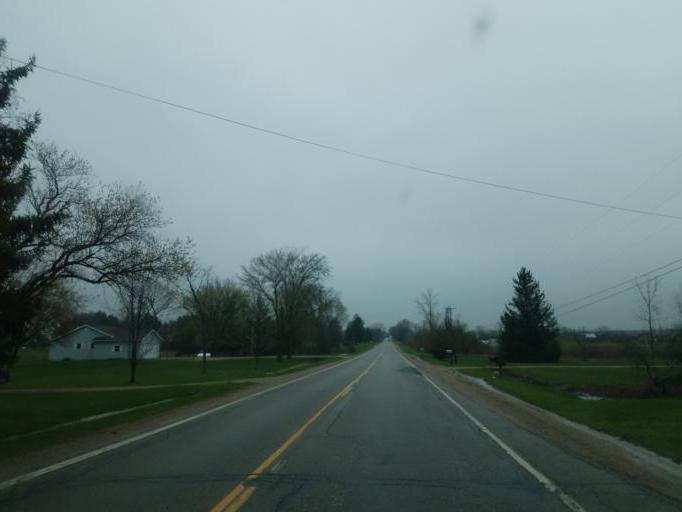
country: US
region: Michigan
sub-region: Isabella County
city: Shepherd
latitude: 43.5241
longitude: -84.7638
